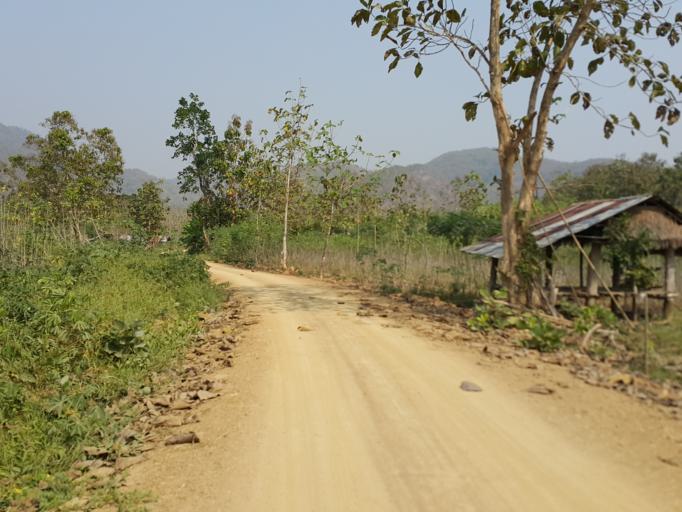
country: TH
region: Sukhothai
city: Thung Saliam
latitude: 17.3389
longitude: 99.4646
